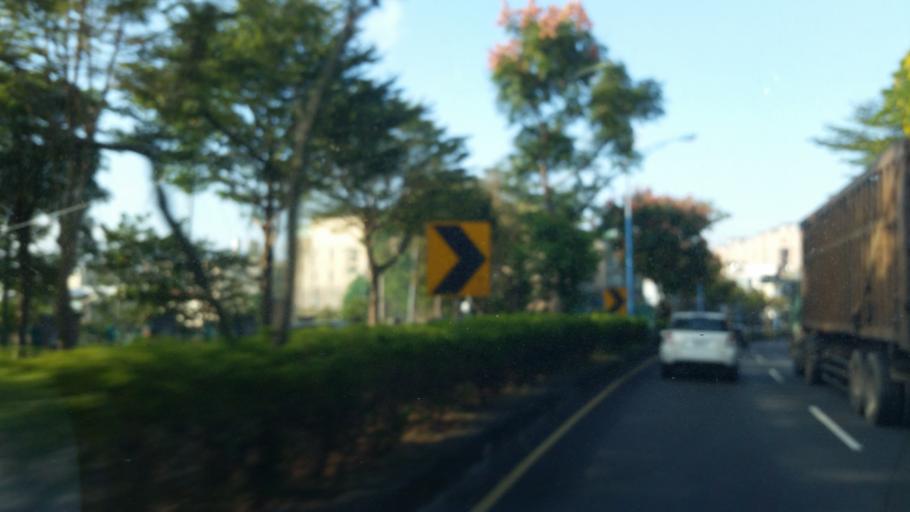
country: TW
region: Taiwan
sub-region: Taoyuan
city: Taoyuan
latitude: 24.9983
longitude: 121.3375
